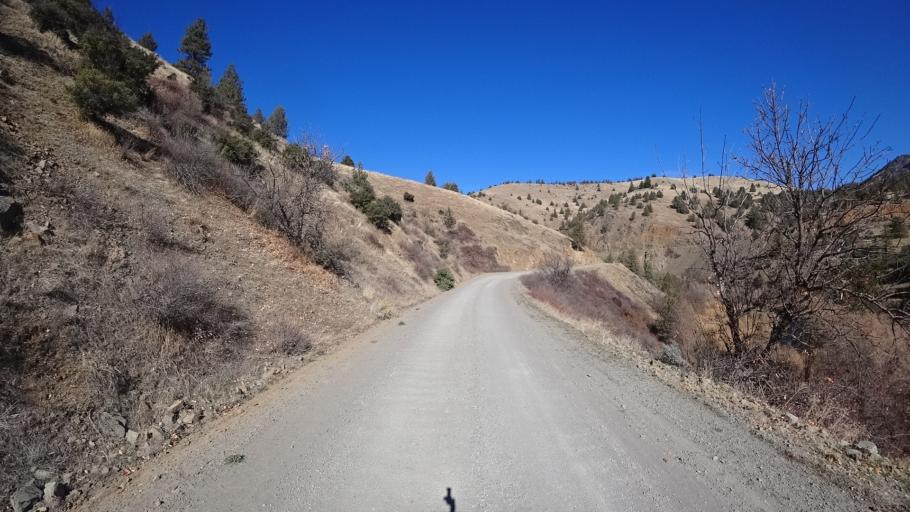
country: US
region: California
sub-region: Siskiyou County
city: Yreka
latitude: 41.7845
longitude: -122.6039
